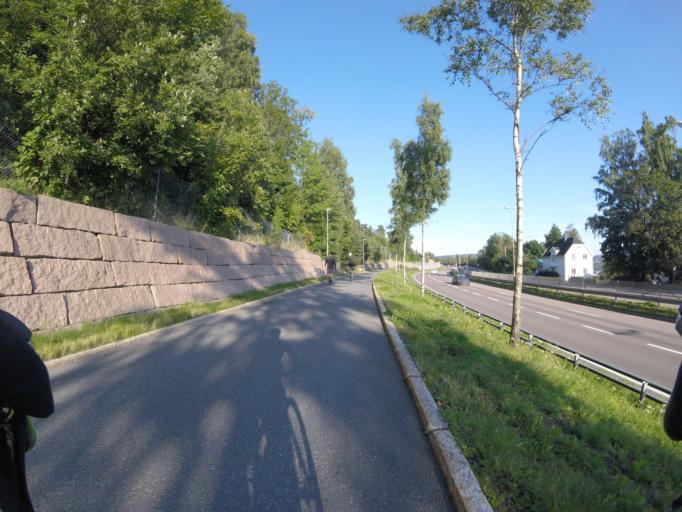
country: NO
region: Oslo
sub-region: Oslo
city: Oslo
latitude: 59.9445
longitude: 10.8221
